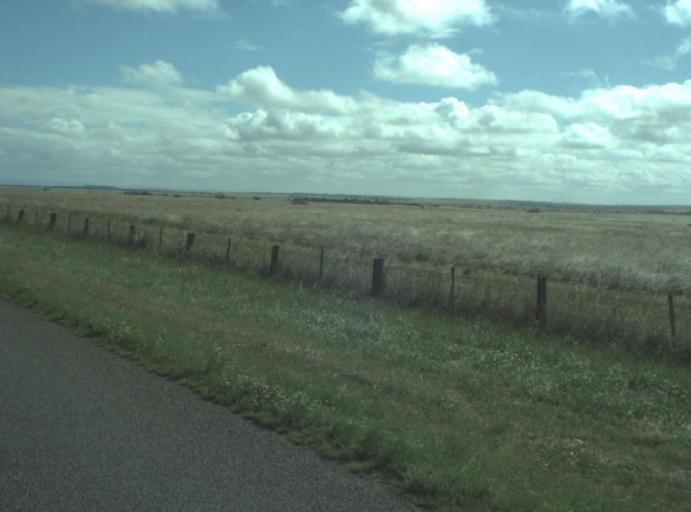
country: AU
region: Victoria
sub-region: Greater Geelong
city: Lara
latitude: -37.9441
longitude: 144.3092
